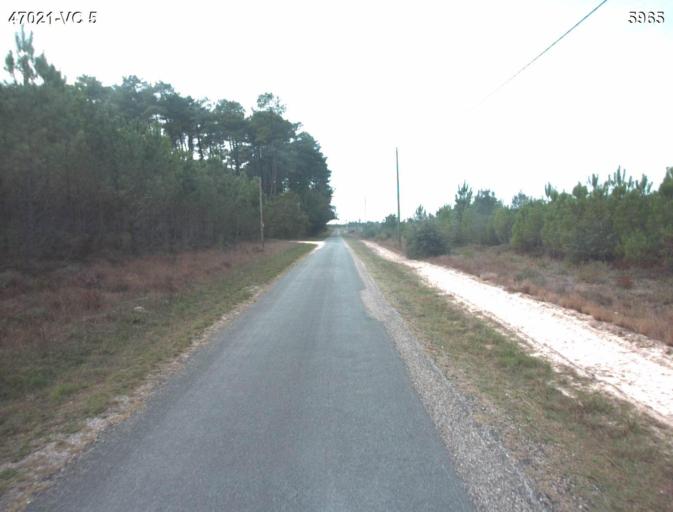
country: FR
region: Aquitaine
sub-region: Departement du Lot-et-Garonne
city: Barbaste
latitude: 44.1495
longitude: 0.2268
